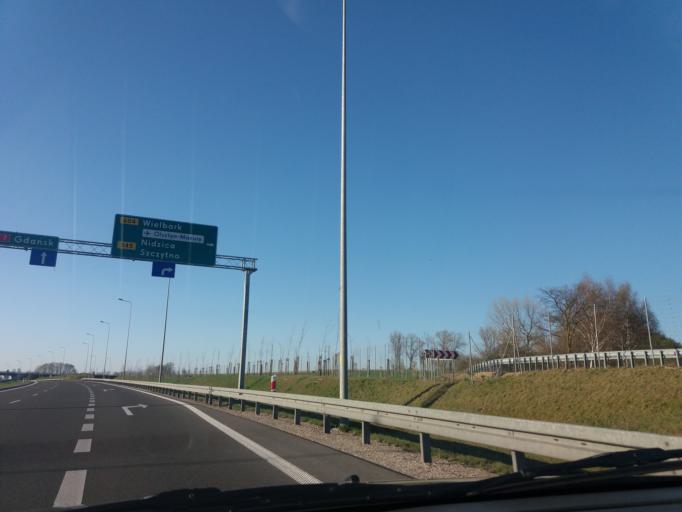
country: PL
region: Warmian-Masurian Voivodeship
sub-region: Powiat nidzicki
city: Nidzica
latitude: 53.3293
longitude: 20.4392
